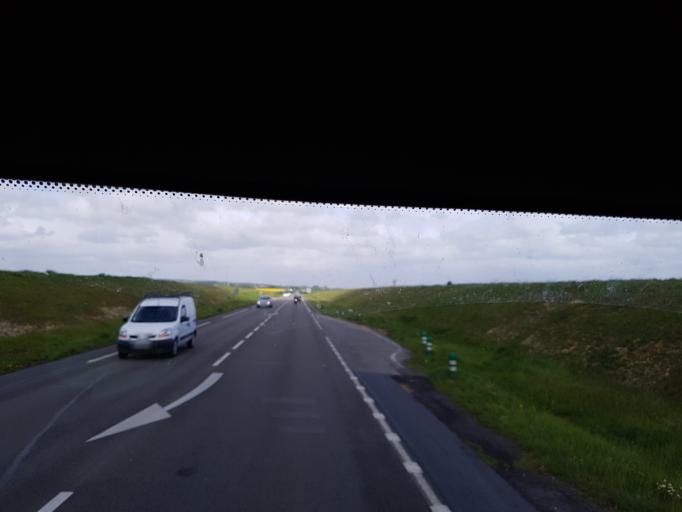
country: FR
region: Nord-Pas-de-Calais
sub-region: Departement du Nord
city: Proville
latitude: 50.1440
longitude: 3.2093
